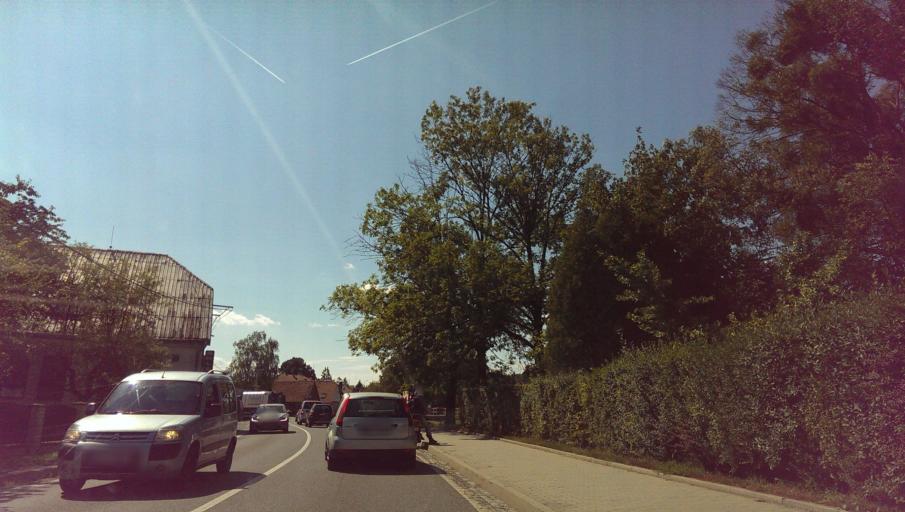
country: CZ
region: Zlin
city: Valasske Mezirici
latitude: 49.4667
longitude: 17.9490
